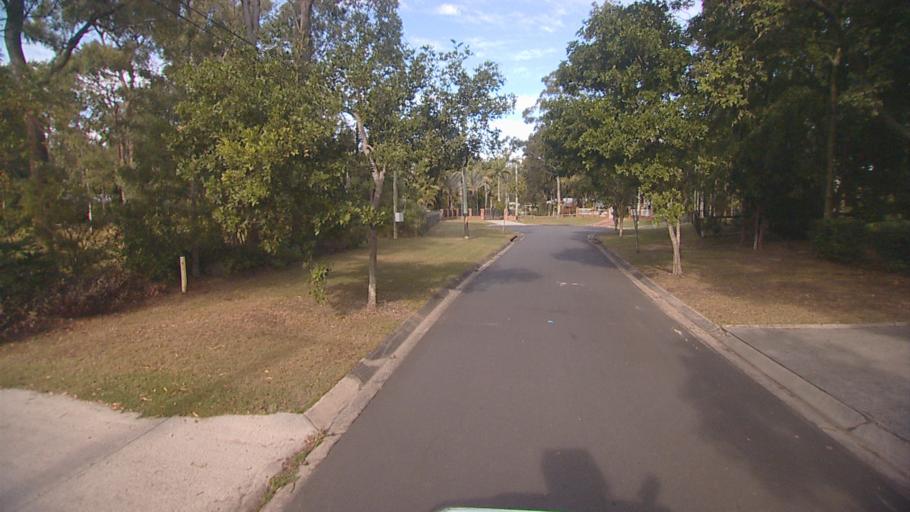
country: AU
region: Queensland
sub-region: Logan
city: Park Ridge South
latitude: -27.6704
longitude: 153.0184
